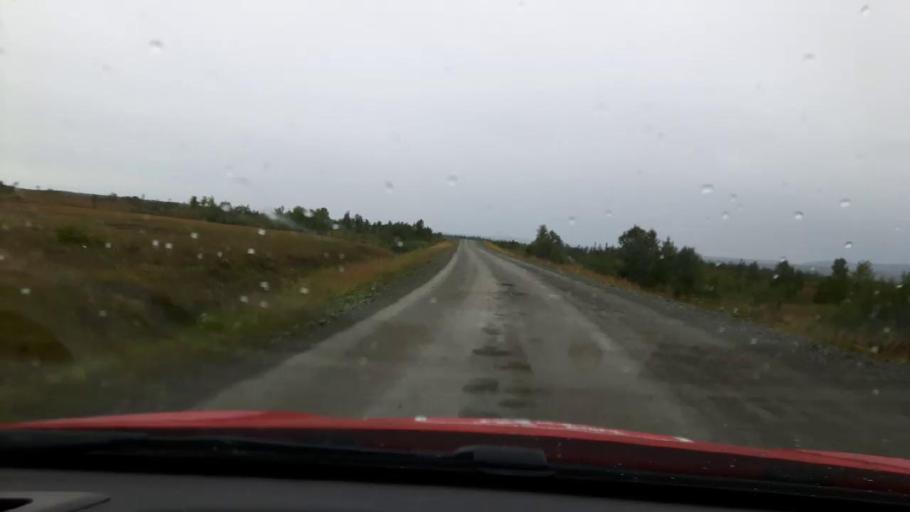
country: NO
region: Nord-Trondelag
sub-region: Meraker
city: Meraker
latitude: 63.6068
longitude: 12.2757
